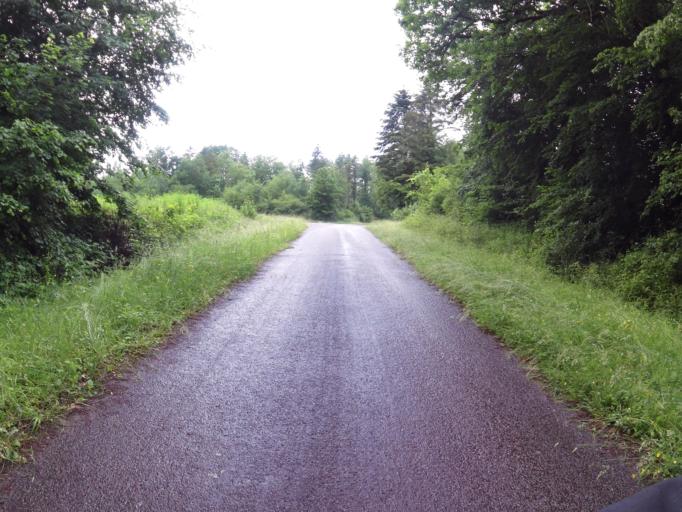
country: FR
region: Champagne-Ardenne
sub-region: Departement de la Marne
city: Sermaize-les-Bains
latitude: 48.7534
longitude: 4.9590
